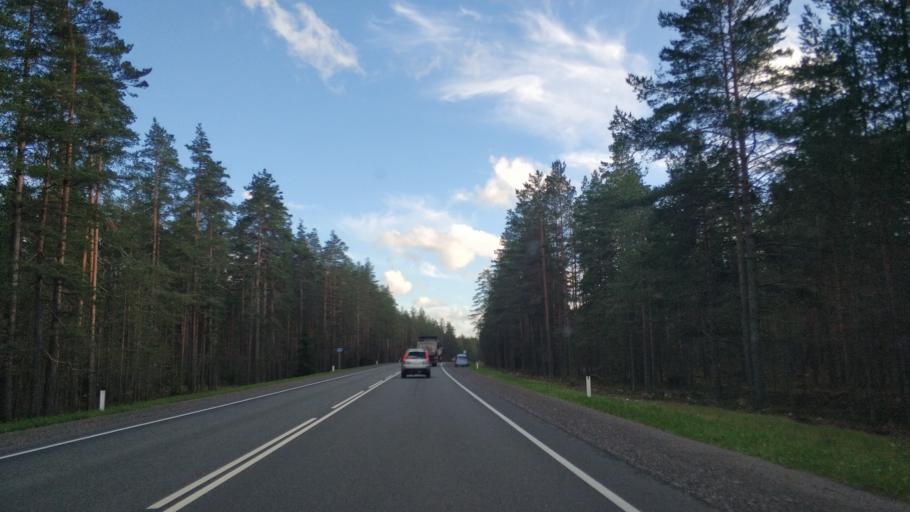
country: RU
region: Leningrad
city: Priozersk
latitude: 60.8872
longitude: 30.1604
